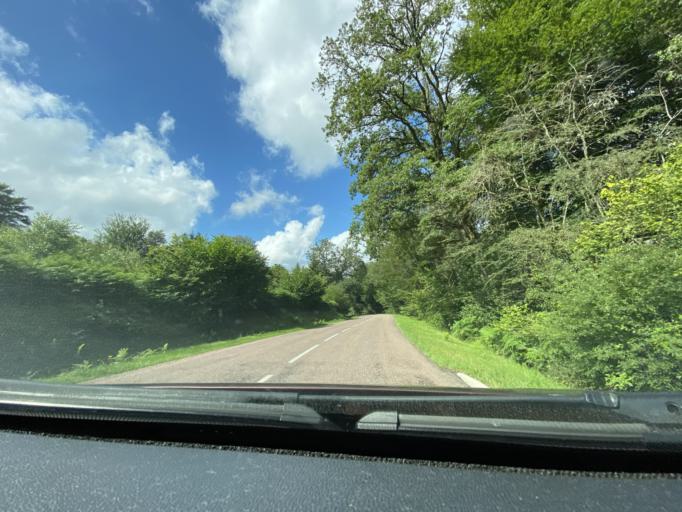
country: FR
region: Bourgogne
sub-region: Departement de la Cote-d'Or
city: Saulieu
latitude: 47.2649
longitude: 4.1237
